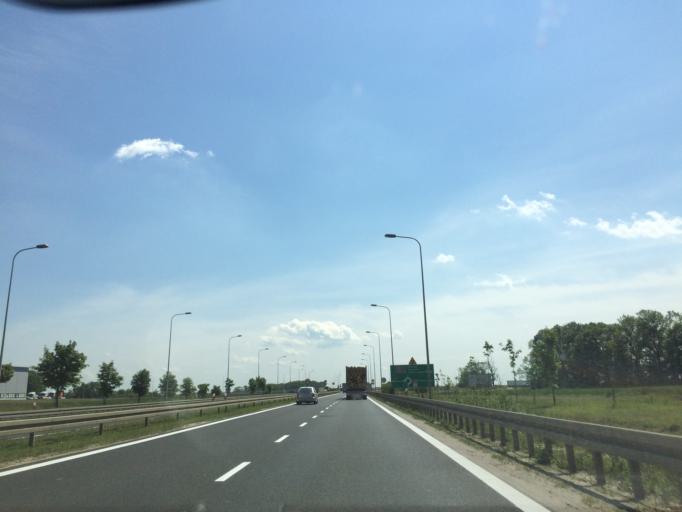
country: PL
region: Lower Silesian Voivodeship
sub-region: Powiat wroclawski
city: Tyniec Maly
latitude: 51.0322
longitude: 16.9282
